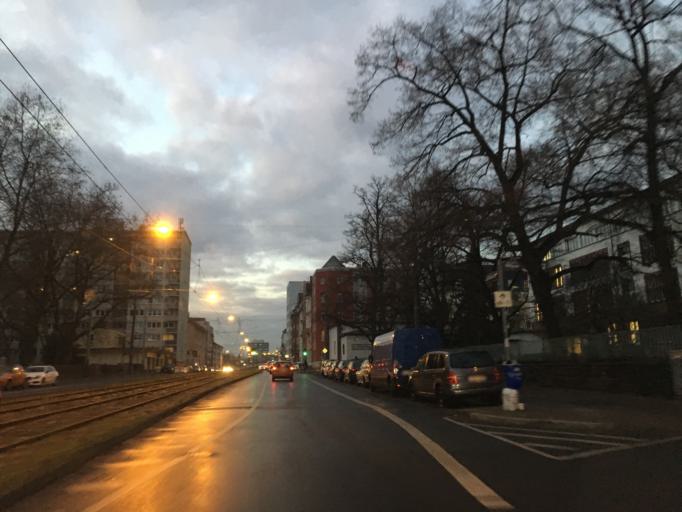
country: DE
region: Hesse
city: Niederrad
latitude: 50.1219
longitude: 8.6391
